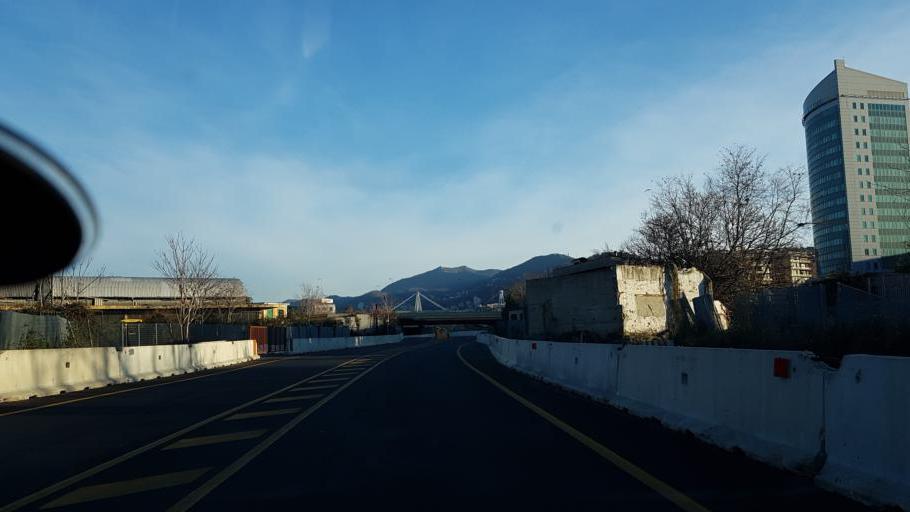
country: IT
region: Liguria
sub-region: Provincia di Genova
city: San Teodoro
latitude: 44.4138
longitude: 8.8774
